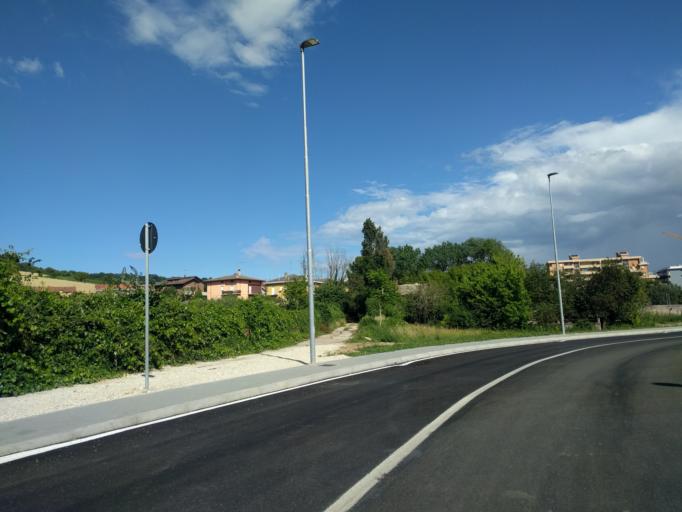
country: IT
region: The Marches
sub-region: Provincia di Pesaro e Urbino
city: Pesaro
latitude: 43.9162
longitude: 12.8607
